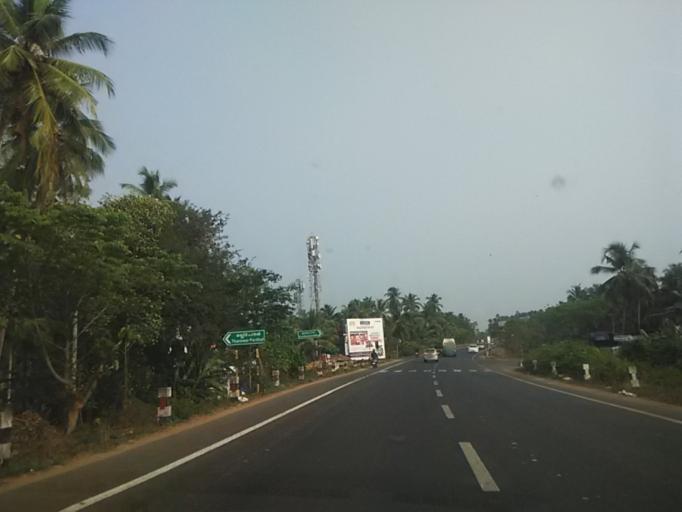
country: IN
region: Kerala
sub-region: Kozhikode
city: Kozhikode
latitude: 11.3116
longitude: 75.7827
